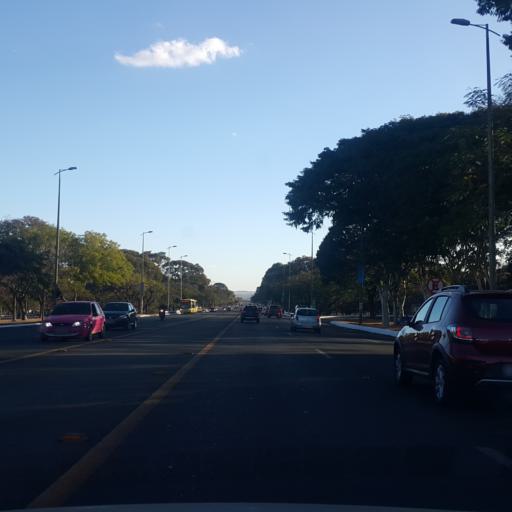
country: BR
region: Federal District
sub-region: Brasilia
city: Brasilia
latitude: -15.8233
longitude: -47.9095
